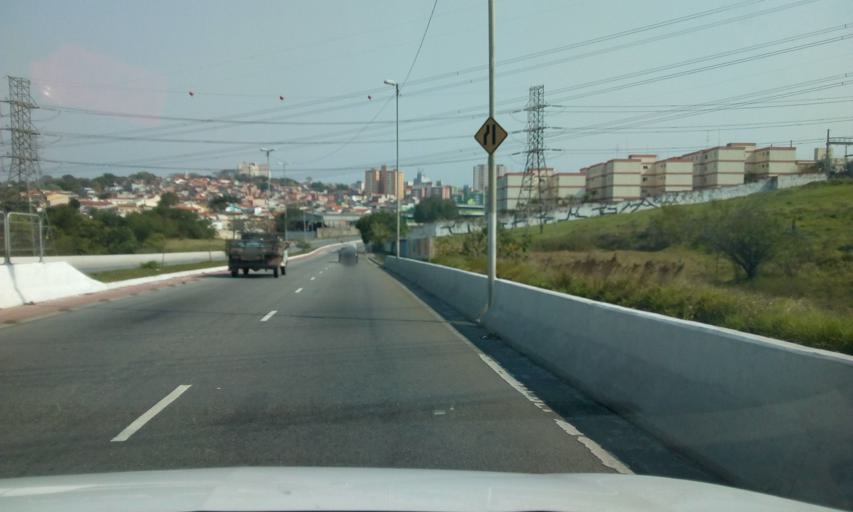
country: BR
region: Sao Paulo
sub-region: Diadema
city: Diadema
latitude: -23.7014
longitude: -46.6851
